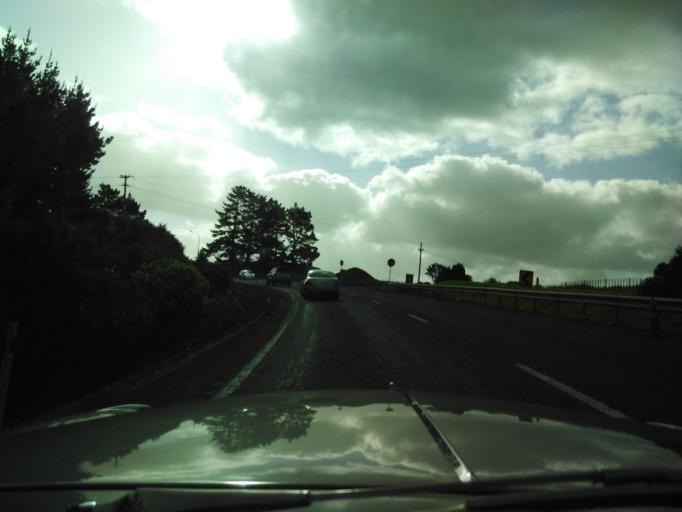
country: NZ
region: Auckland
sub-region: Auckland
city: Wellsford
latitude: -36.2241
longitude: 174.4893
